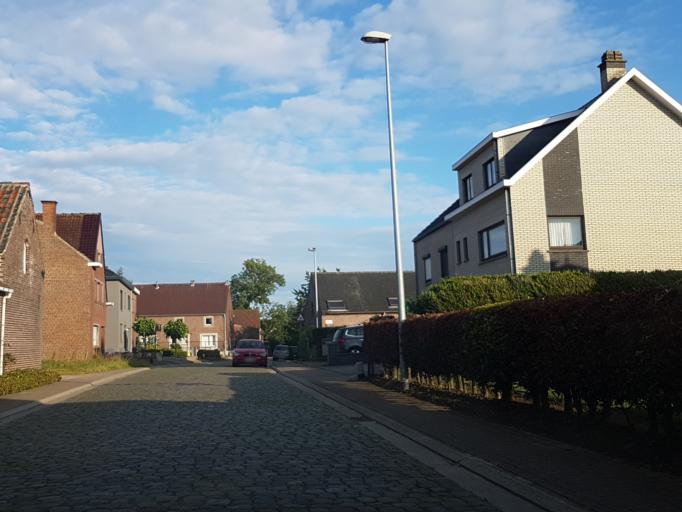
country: BE
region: Flanders
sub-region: Provincie Oost-Vlaanderen
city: Lebbeke
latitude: 50.9464
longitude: 4.1136
